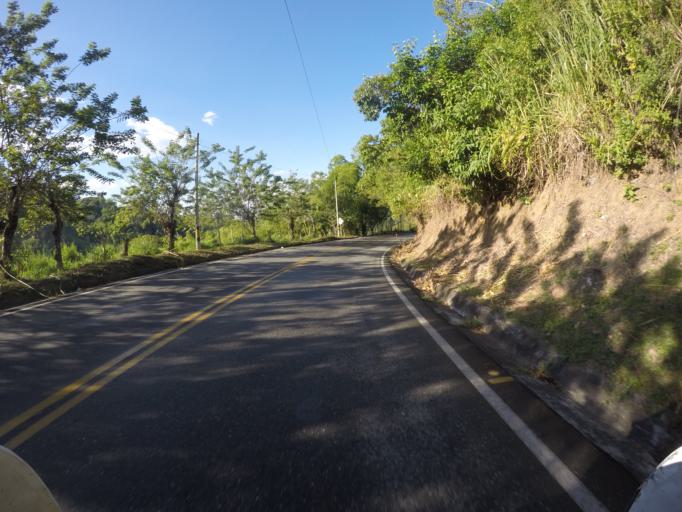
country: CO
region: Valle del Cauca
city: Cartago
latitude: 4.7179
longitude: -75.8604
